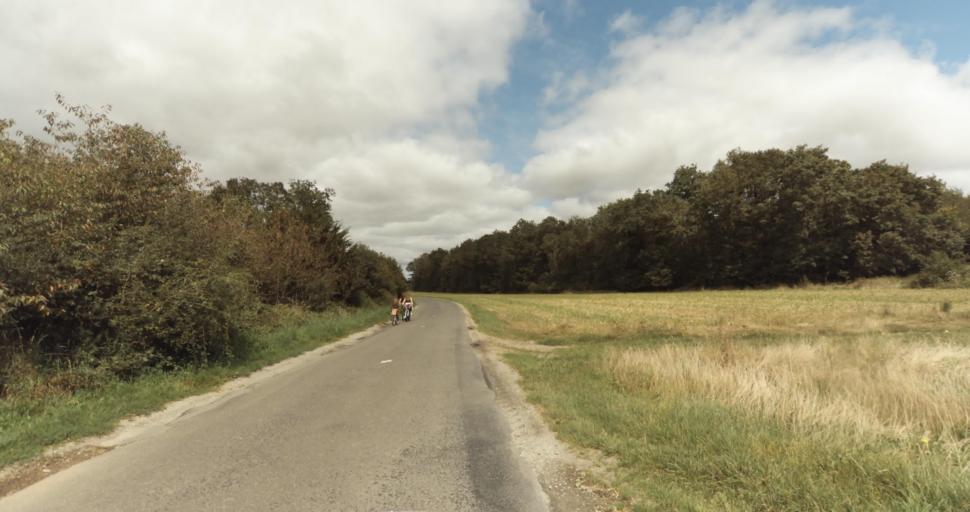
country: FR
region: Haute-Normandie
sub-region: Departement de l'Eure
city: Evreux
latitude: 48.9282
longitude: 1.2029
